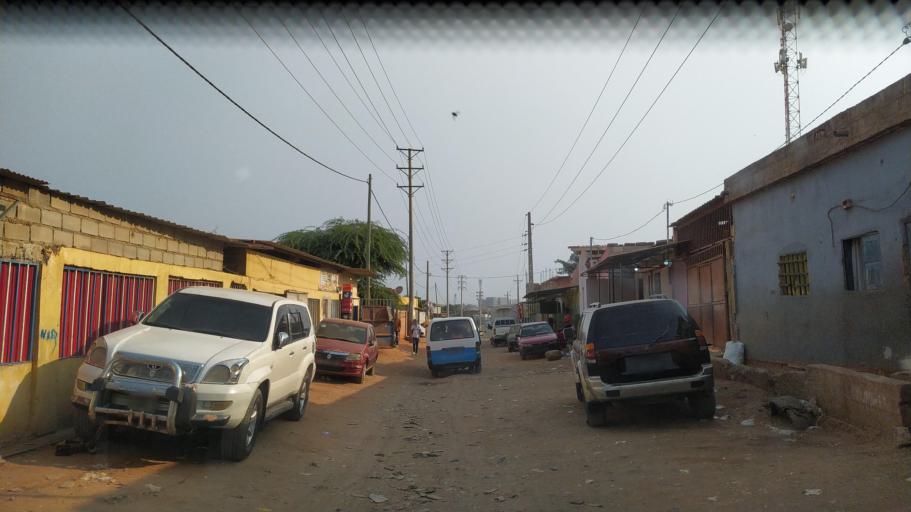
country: AO
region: Luanda
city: Luanda
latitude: -8.8686
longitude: 13.2003
